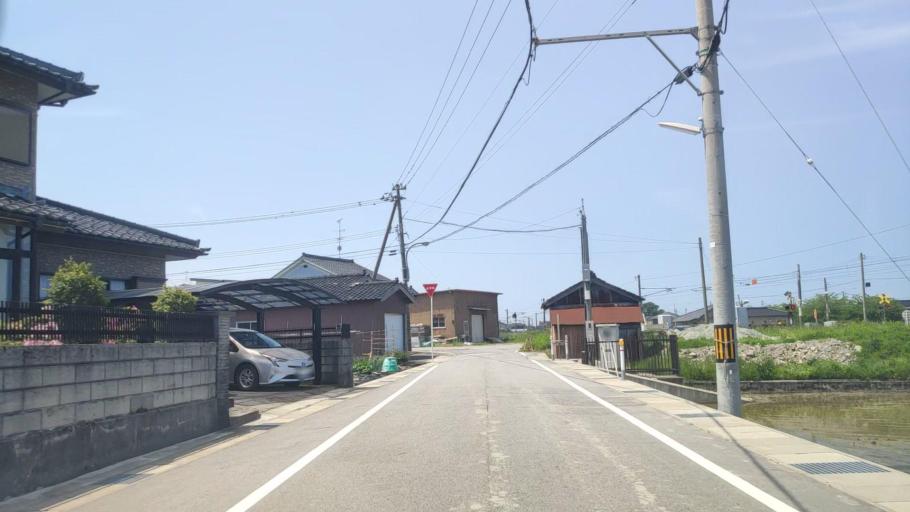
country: JP
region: Toyama
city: Nyuzen
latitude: 36.9535
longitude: 137.5659
